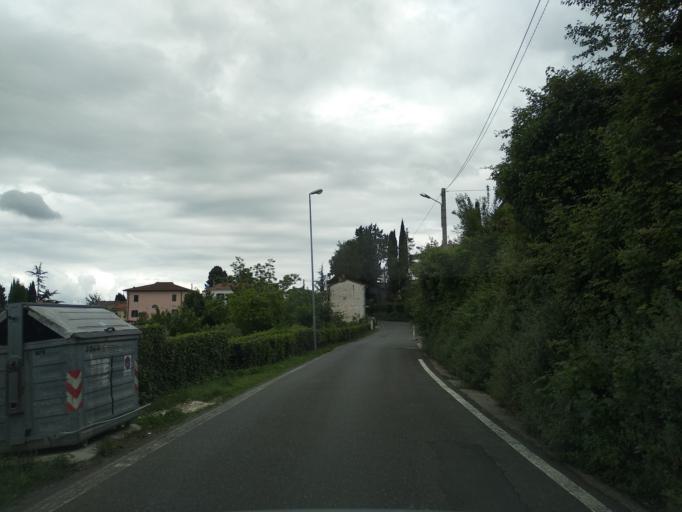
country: IT
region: Tuscany
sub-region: Provincia di Livorno
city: Collesalvetti
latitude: 43.5430
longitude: 10.4369
